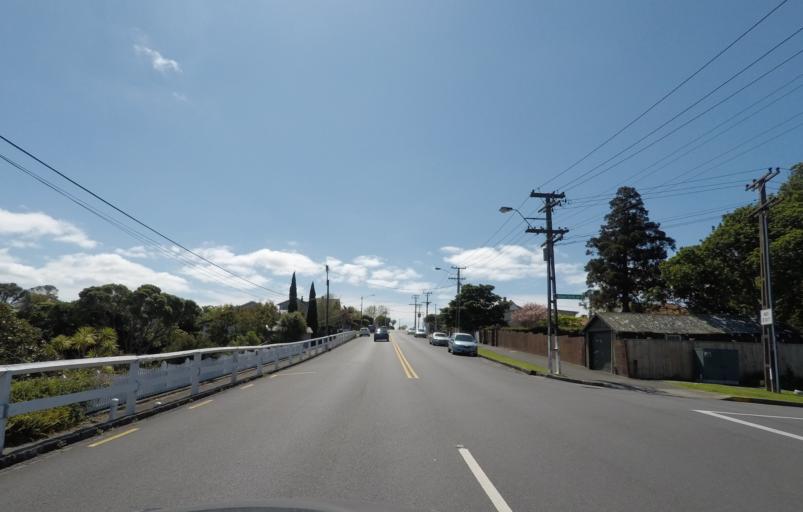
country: NZ
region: Auckland
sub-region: Auckland
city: Auckland
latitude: -36.8856
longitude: 174.8092
